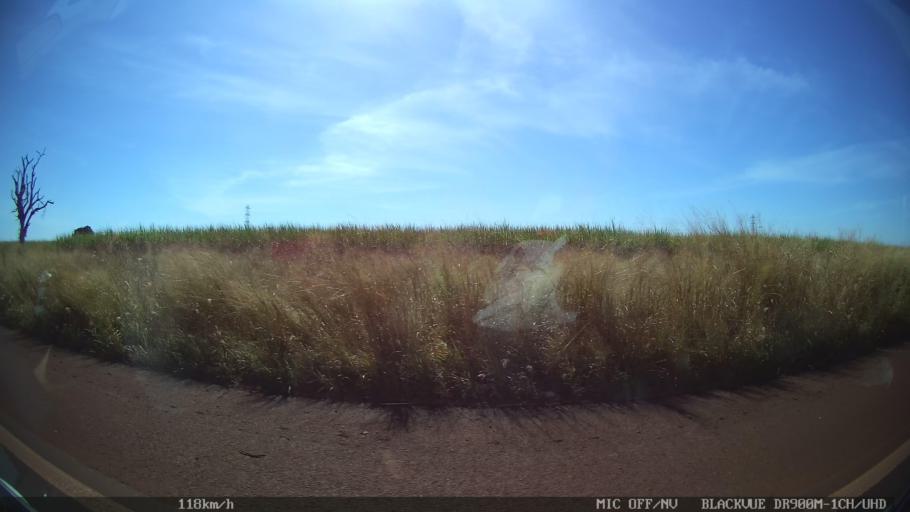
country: BR
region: Sao Paulo
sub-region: Guaira
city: Guaira
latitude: -20.4452
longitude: -48.3938
